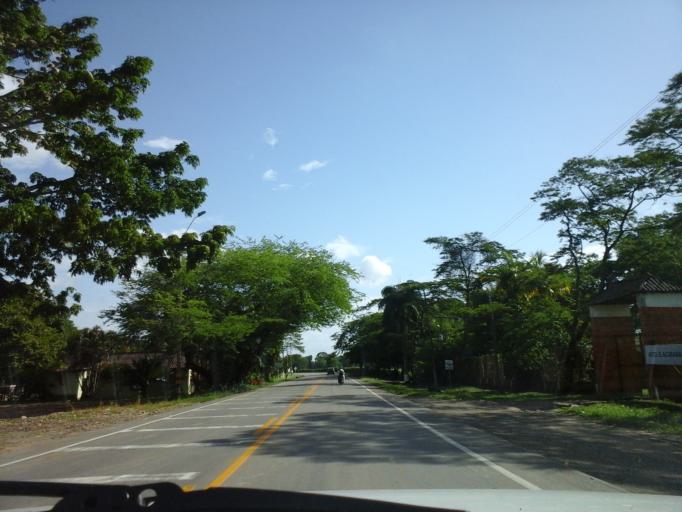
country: CO
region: Meta
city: Cumaral
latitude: 4.0933
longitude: -73.3551
